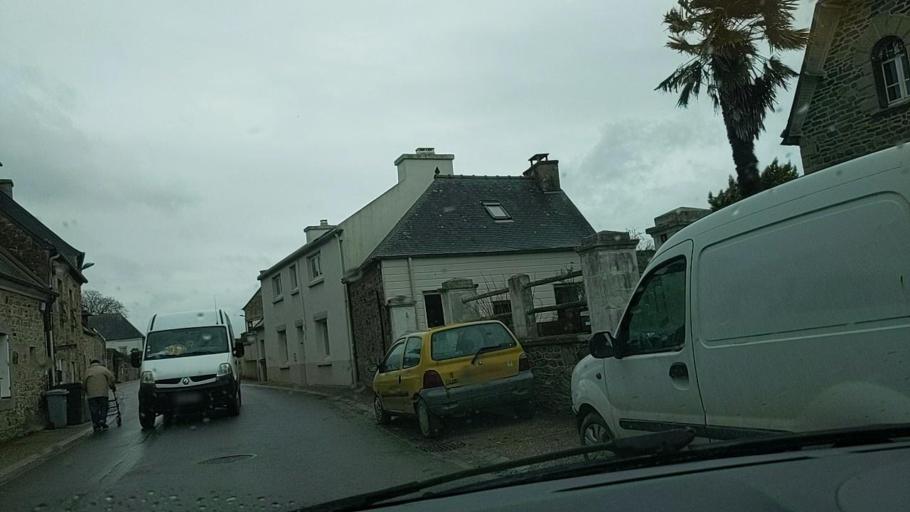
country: FR
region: Brittany
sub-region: Departement des Cotes-d'Armor
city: Pleumeur-Gautier
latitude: 48.8038
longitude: -3.1589
